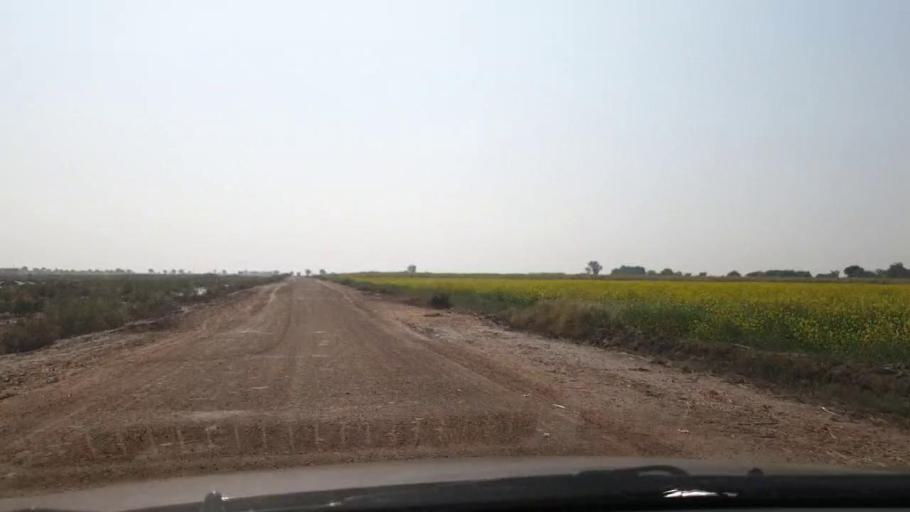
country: PK
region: Sindh
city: Jhol
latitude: 25.8686
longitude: 68.9980
